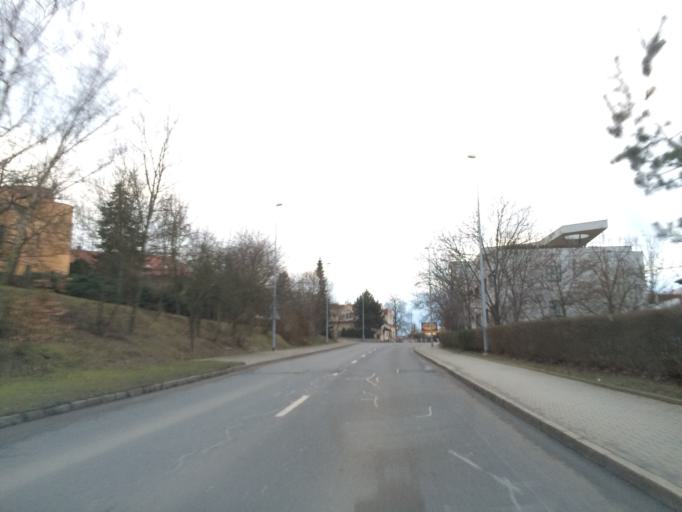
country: CZ
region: Praha
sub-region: Praha 1
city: Mala Strana
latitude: 50.1128
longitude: 14.3834
